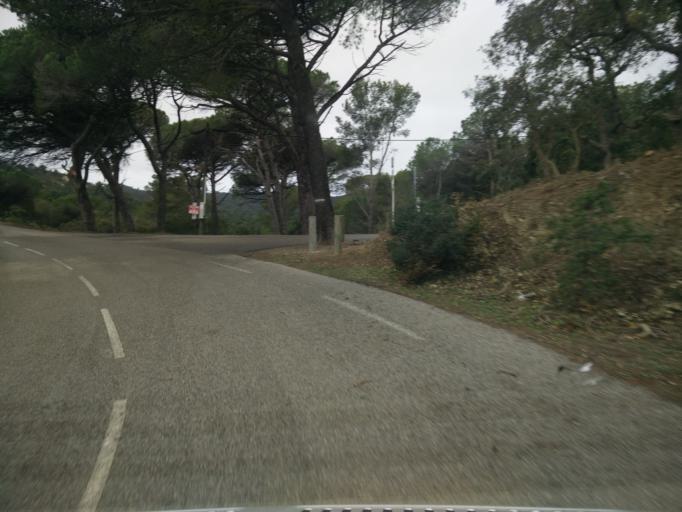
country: FR
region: Provence-Alpes-Cote d'Azur
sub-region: Departement du Var
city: Six-Fours-les-Plages
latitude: 43.0632
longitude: 5.8460
